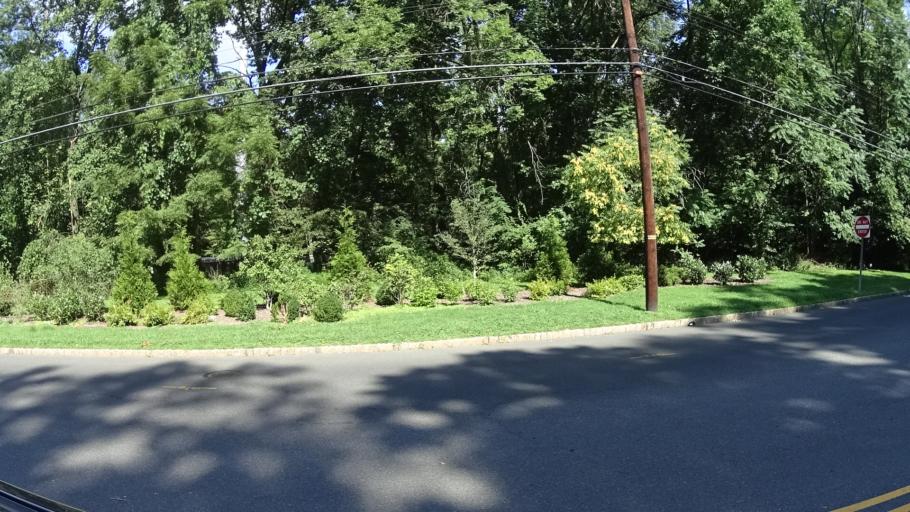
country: US
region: New Jersey
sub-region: Union County
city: New Providence
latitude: 40.7155
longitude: -74.3842
